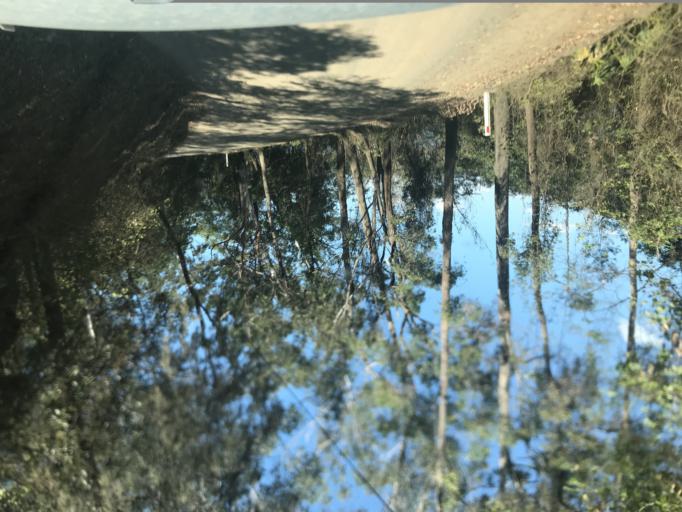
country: AU
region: New South Wales
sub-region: Hawkesbury
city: Pitt Town
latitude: -33.4183
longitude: 150.9009
